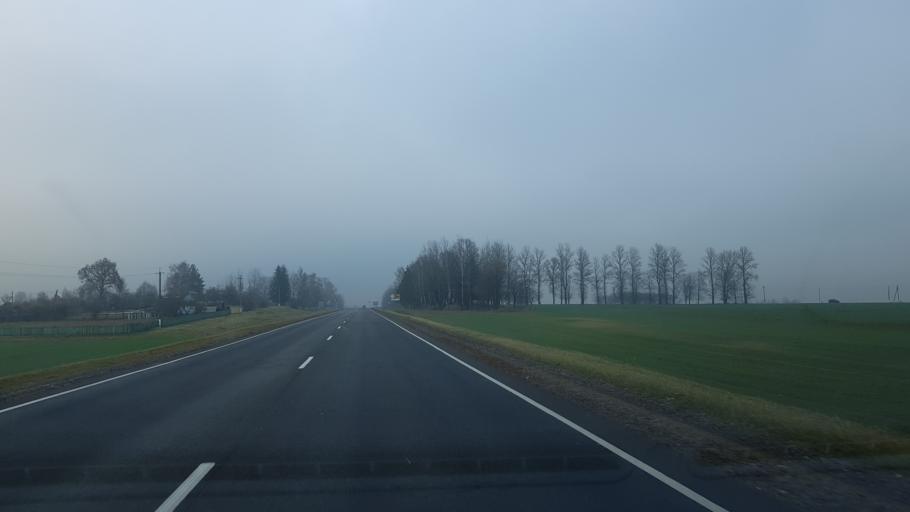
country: BY
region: Mogilev
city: Babruysk
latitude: 53.1755
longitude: 29.3430
